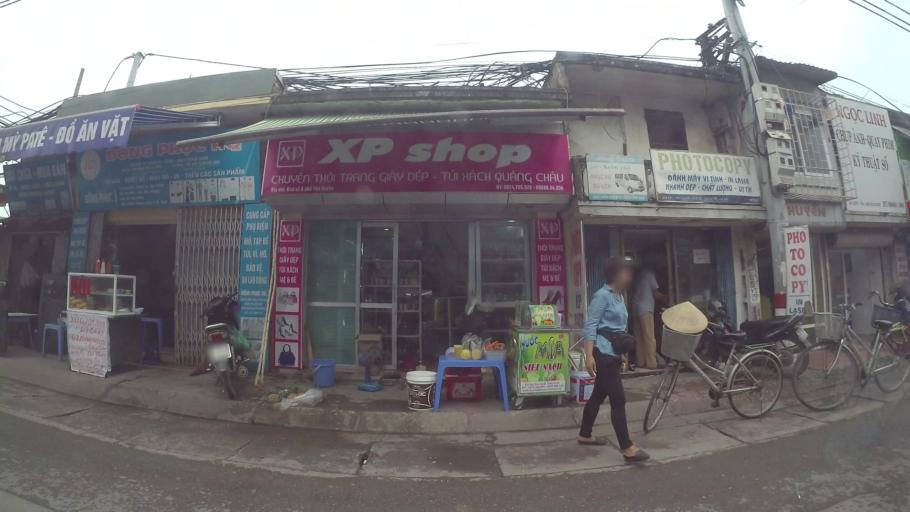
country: VN
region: Ha Noi
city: Van Dien
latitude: 20.9681
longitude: 105.8717
